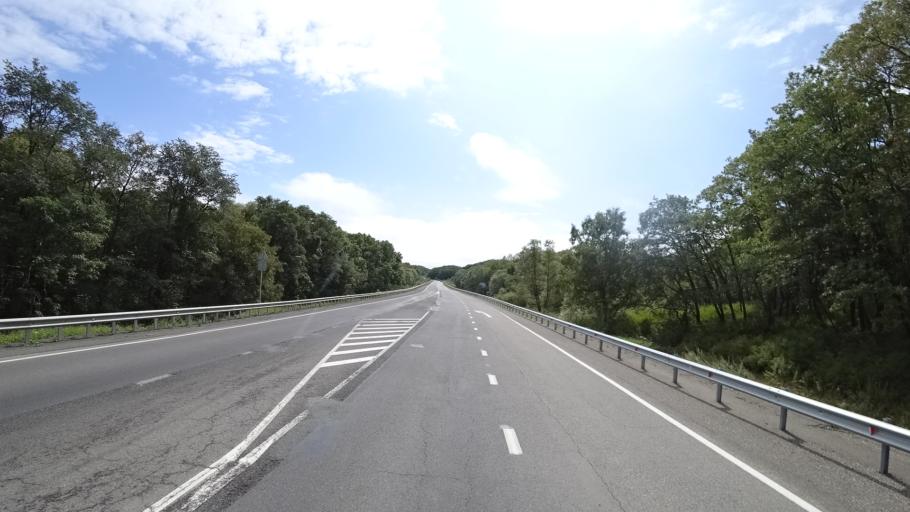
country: RU
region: Primorskiy
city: Lyalichi
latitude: 44.1377
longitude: 132.4285
